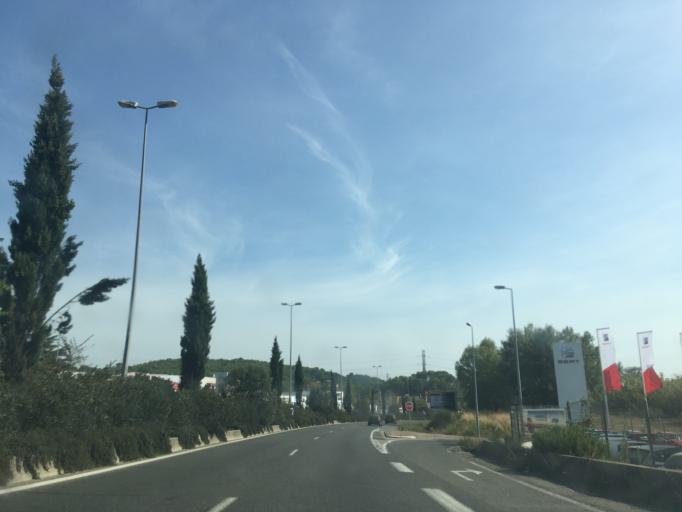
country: FR
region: Provence-Alpes-Cote d'Azur
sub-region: Departement du Var
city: Trans-en-Provence
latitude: 43.5169
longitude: 6.4741
